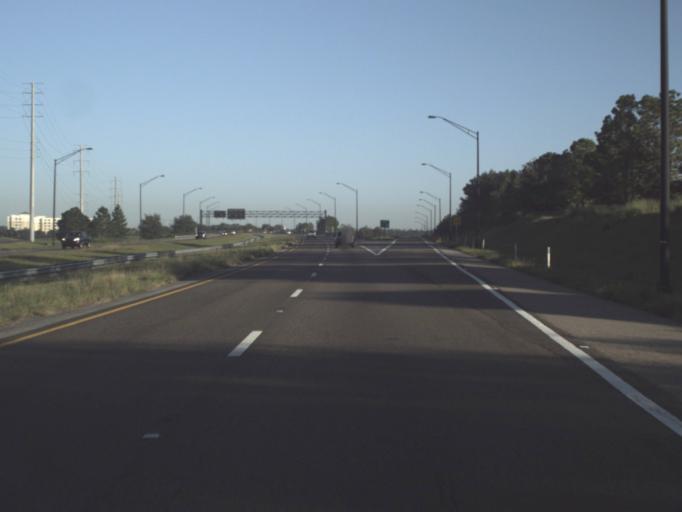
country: US
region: Florida
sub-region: Polk County
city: Citrus Ridge
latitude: 28.3716
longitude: -81.6099
